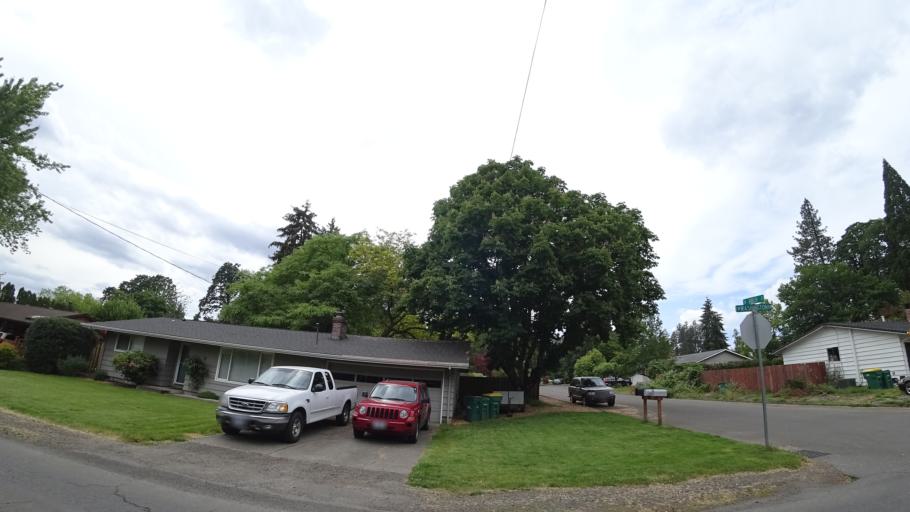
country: US
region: Oregon
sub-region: Washington County
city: Metzger
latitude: 45.4534
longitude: -122.7660
